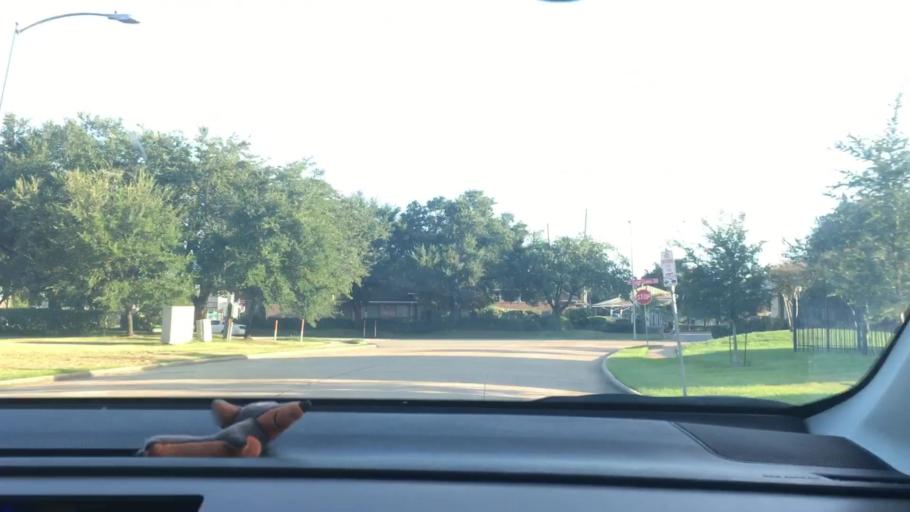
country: US
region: Texas
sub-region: Fort Bend County
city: Meadows Place
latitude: 29.6439
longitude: -95.5848
